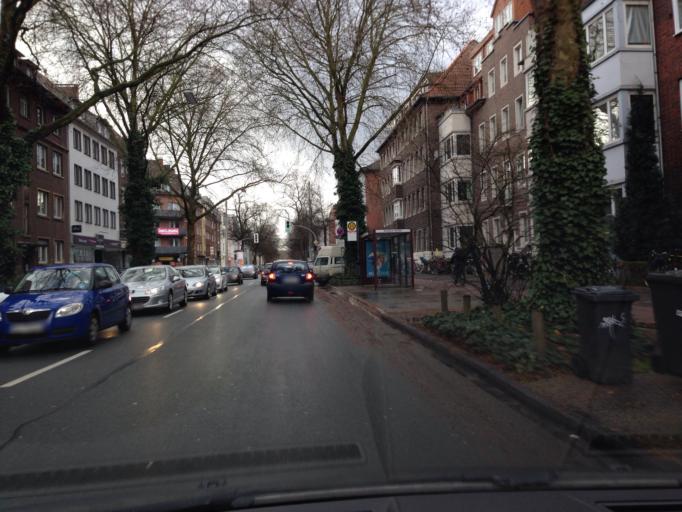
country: DE
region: North Rhine-Westphalia
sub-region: Regierungsbezirk Munster
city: Muenster
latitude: 51.9533
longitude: 7.6429
